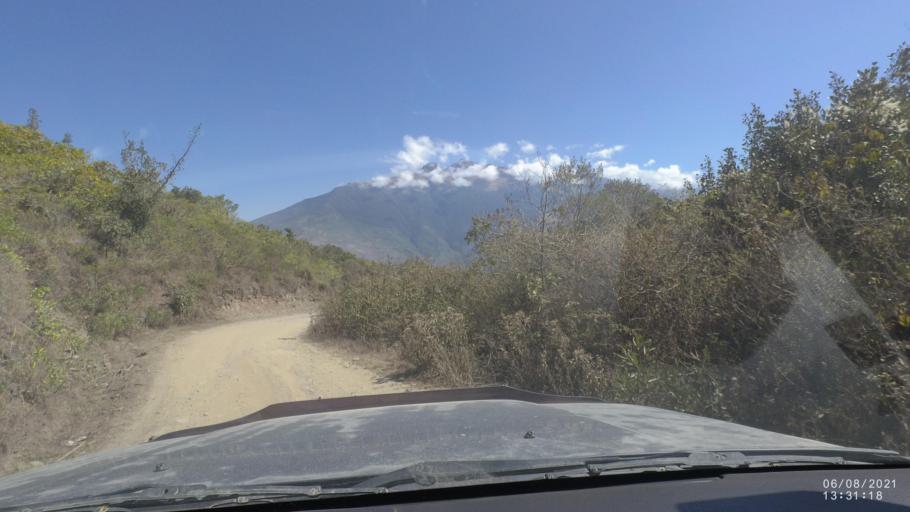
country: BO
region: La Paz
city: Quime
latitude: -16.7009
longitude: -66.7266
